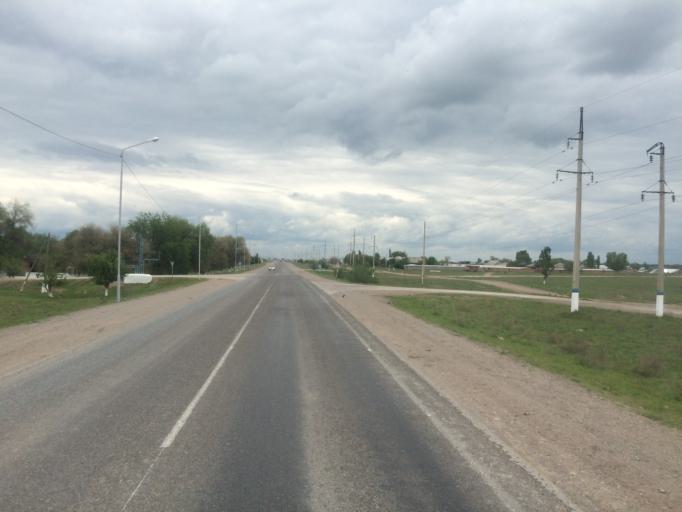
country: KG
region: Chuy
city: Sokuluk
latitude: 43.2506
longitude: 74.2875
